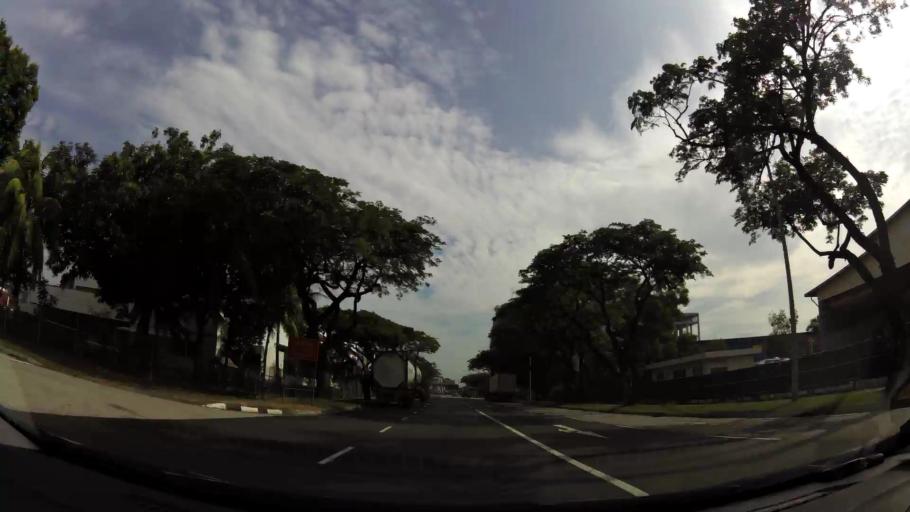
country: MY
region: Johor
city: Johor Bahru
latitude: 1.3124
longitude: 103.6539
